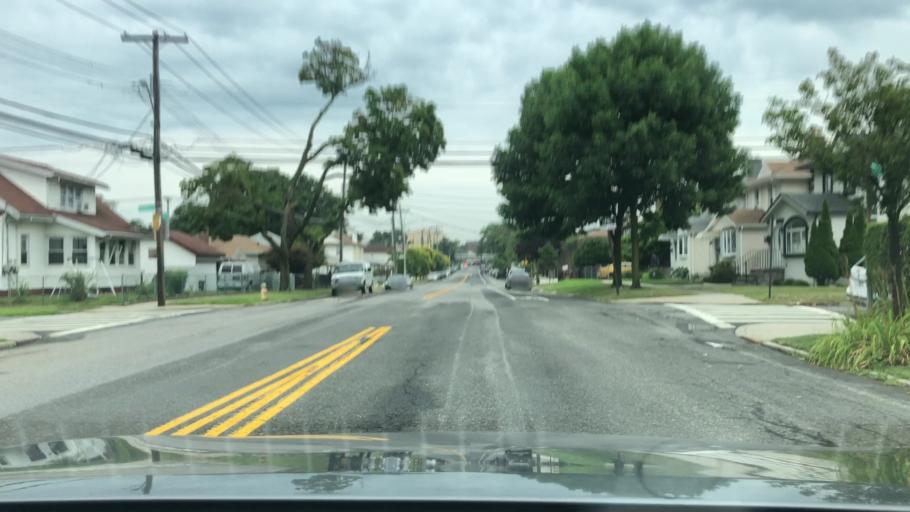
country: US
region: New York
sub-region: Nassau County
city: Bellerose Terrace
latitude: 40.7153
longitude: -73.7309
